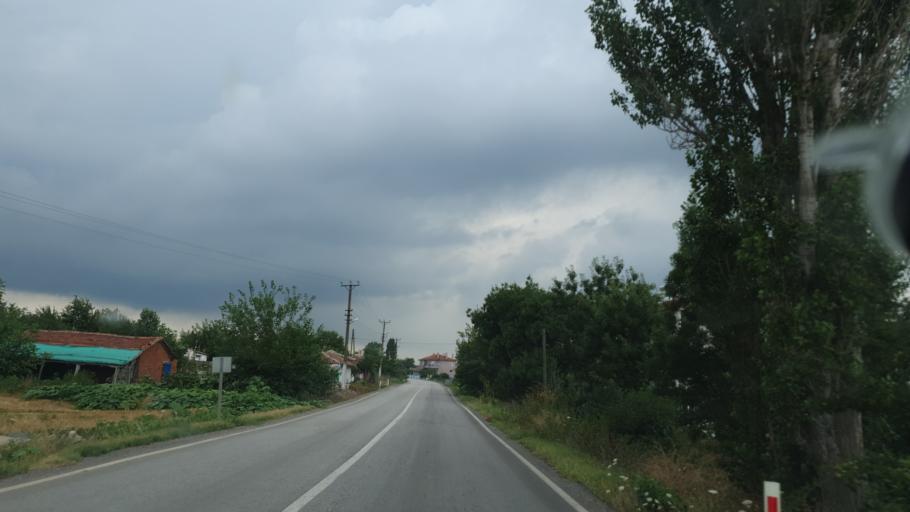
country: TR
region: Tekirdag
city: Hayrabolu
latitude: 41.2200
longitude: 26.9869
